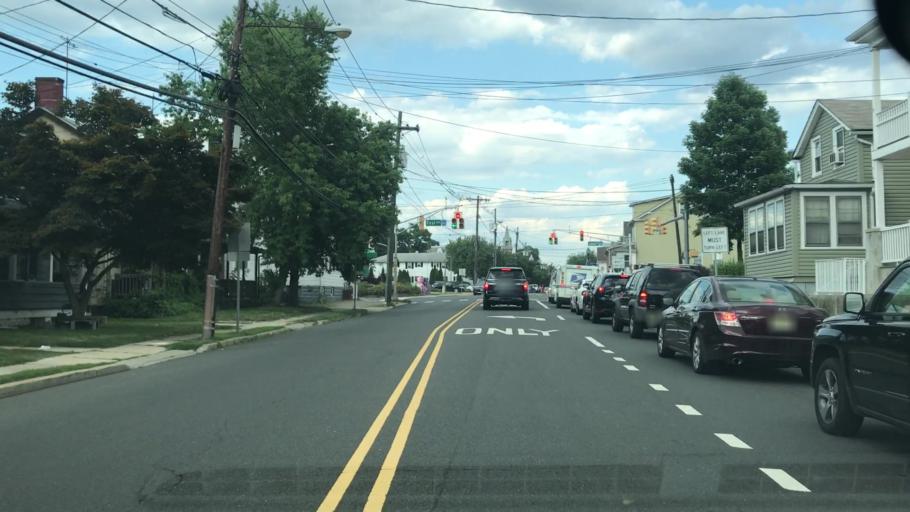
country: US
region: New Jersey
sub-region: Somerset County
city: Raritan
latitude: 40.5659
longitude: -74.6383
